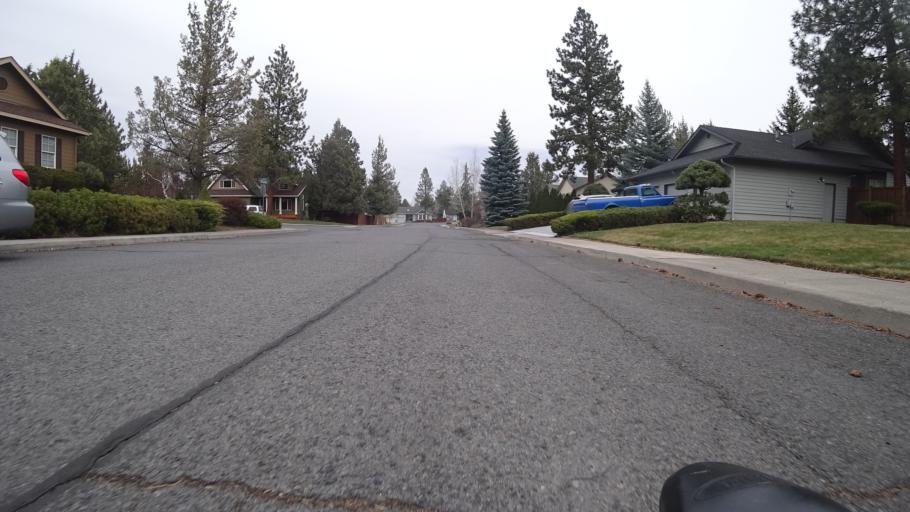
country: US
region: Oregon
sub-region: Deschutes County
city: Bend
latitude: 44.0407
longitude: -121.2771
